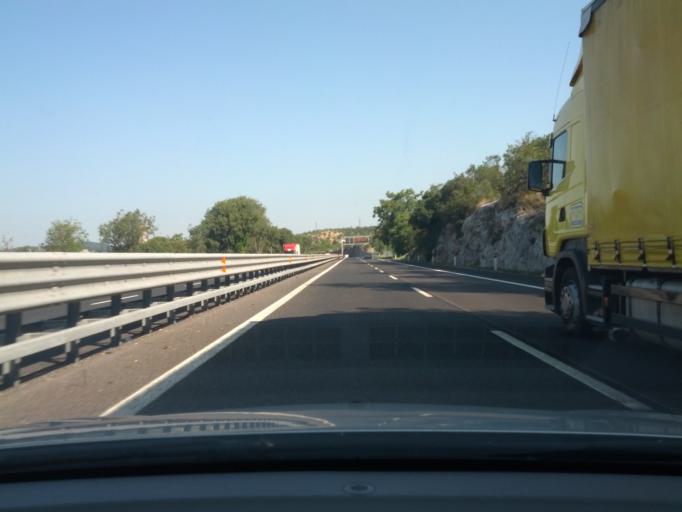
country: IT
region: Friuli Venezia Giulia
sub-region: Provincia di Trieste
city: Duino
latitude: 45.7856
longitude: 13.5957
